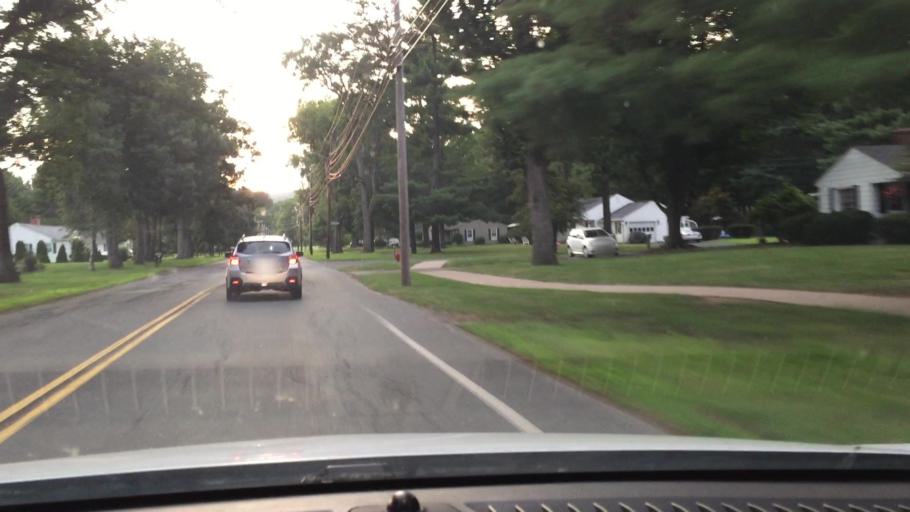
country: US
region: Massachusetts
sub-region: Hampden County
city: Westfield
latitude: 42.1317
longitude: -72.8014
